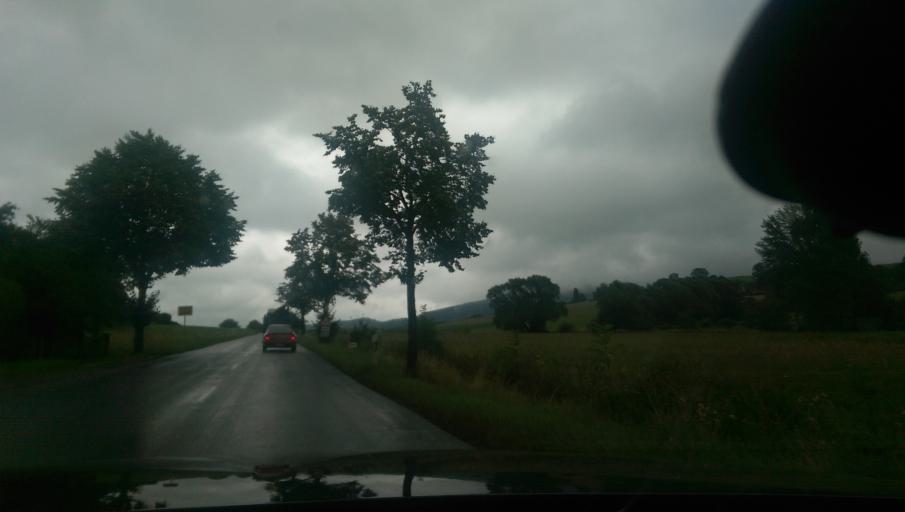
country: DE
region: Hesse
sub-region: Regierungsbezirk Kassel
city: Grossalmerode
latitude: 51.2157
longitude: 9.7979
